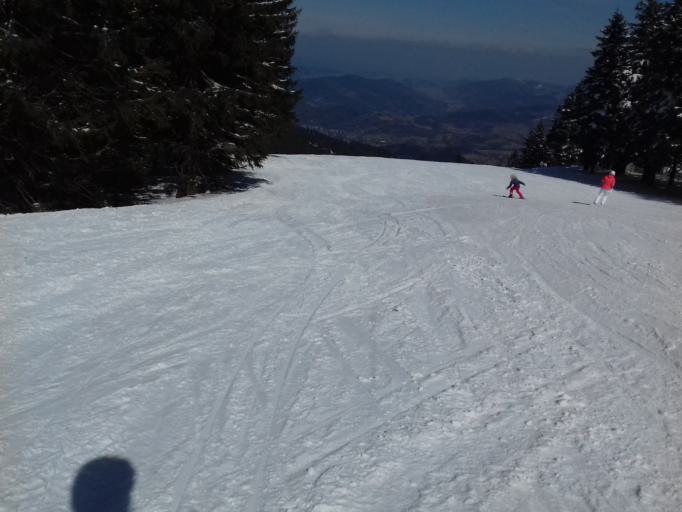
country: PL
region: Silesian Voivodeship
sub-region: Powiat zywiecki
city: Korbielow
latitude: 49.5384
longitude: 19.3194
